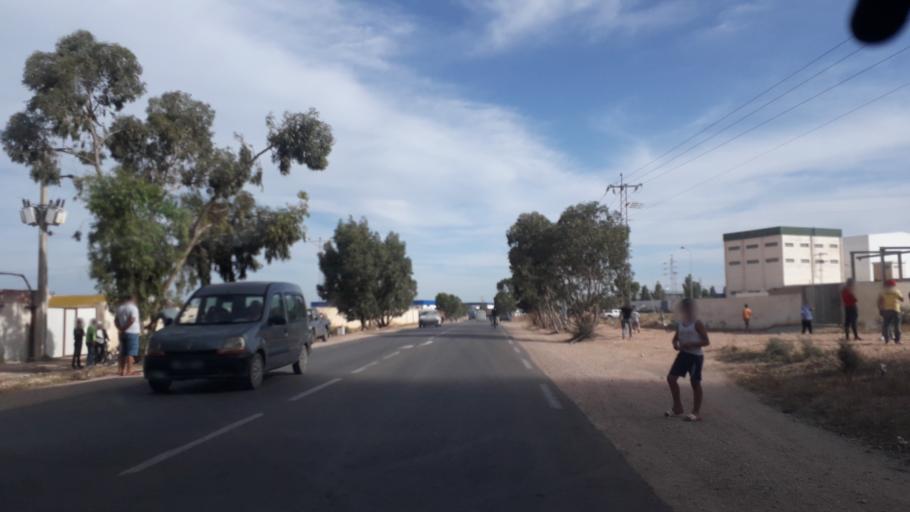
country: TN
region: Safaqis
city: Al Qarmadah
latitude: 34.8937
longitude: 10.7623
